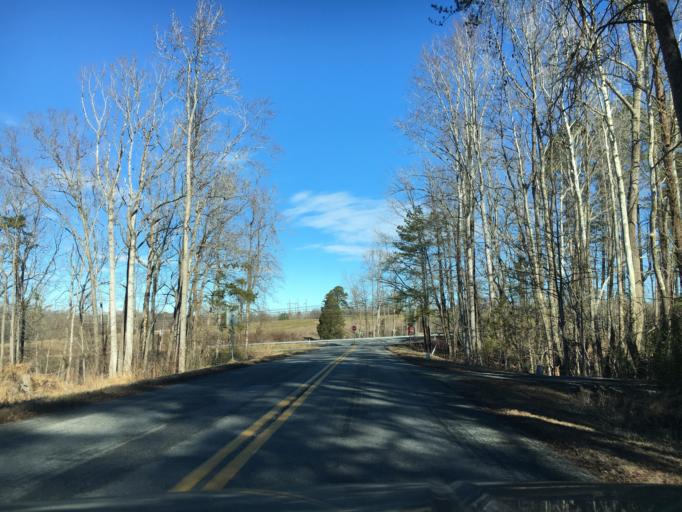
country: US
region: Virginia
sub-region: Halifax County
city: South Boston
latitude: 36.7110
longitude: -78.8720
